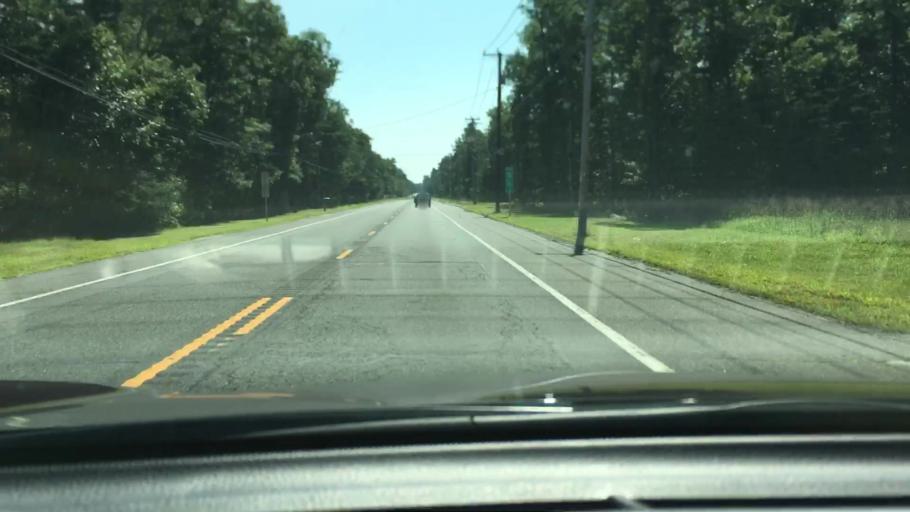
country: US
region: New Jersey
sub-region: Cumberland County
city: Laurel Lake
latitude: 39.3792
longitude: -74.9646
